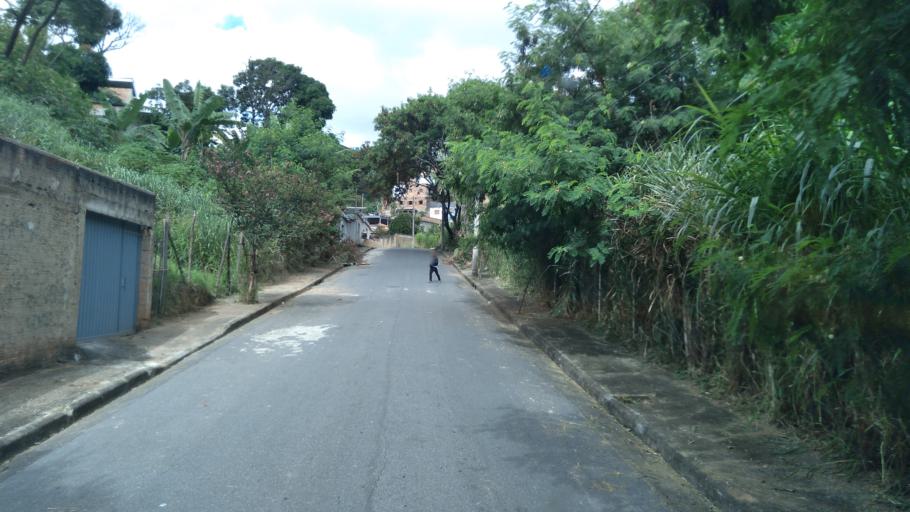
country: BR
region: Minas Gerais
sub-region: Belo Horizonte
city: Belo Horizonte
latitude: -19.8597
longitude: -43.9120
